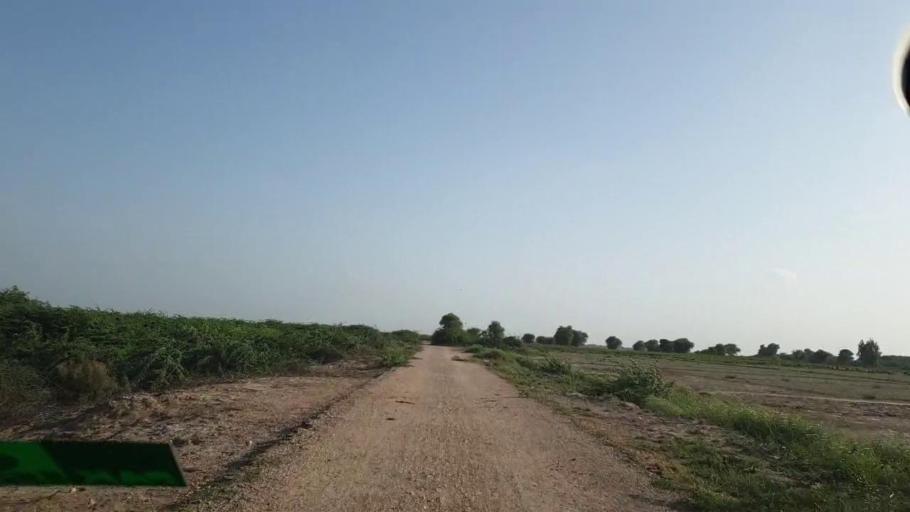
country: PK
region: Sindh
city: Naukot
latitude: 24.7221
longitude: 69.2517
